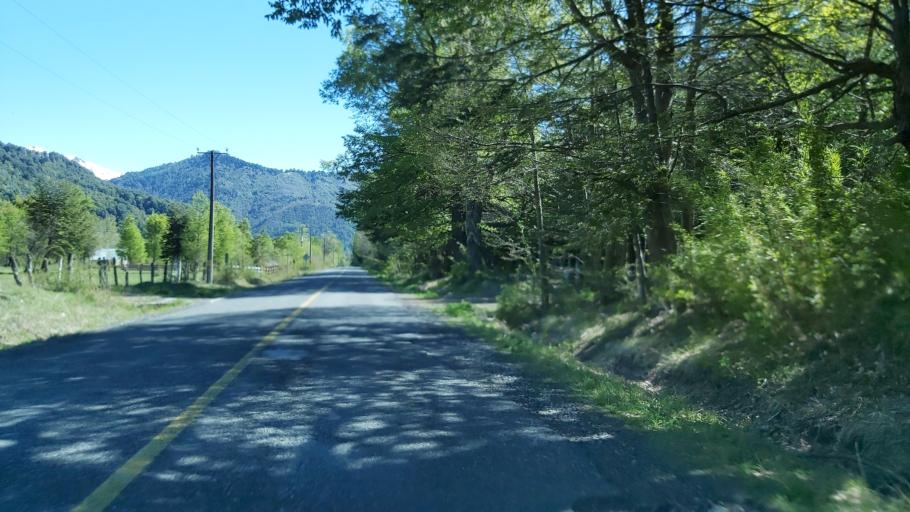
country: CL
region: Araucania
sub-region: Provincia de Cautin
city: Vilcun
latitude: -38.4734
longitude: -71.5280
